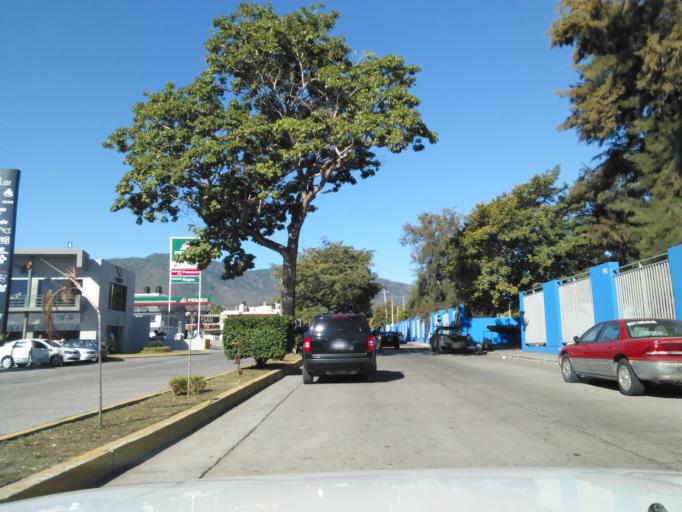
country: MX
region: Nayarit
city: Tepic
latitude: 21.4878
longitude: -104.8901
